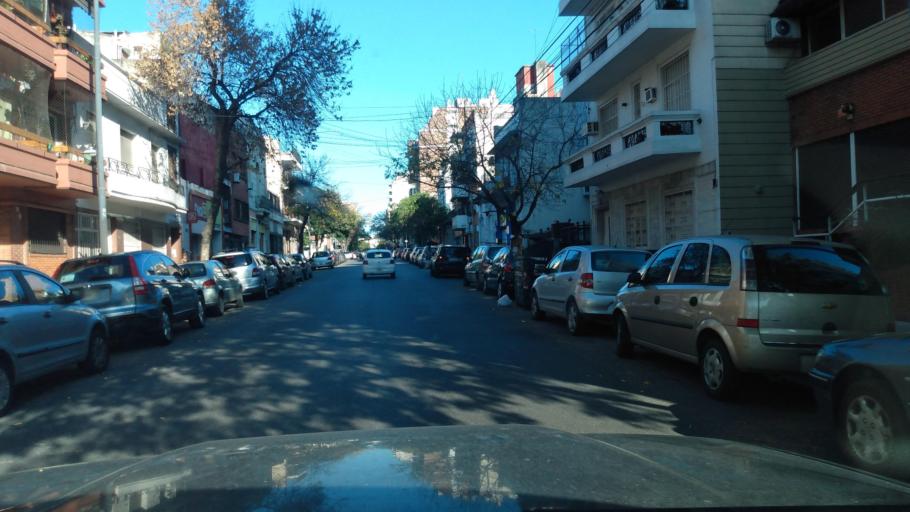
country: AR
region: Buenos Aires F.D.
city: Colegiales
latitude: -34.6037
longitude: -58.4406
